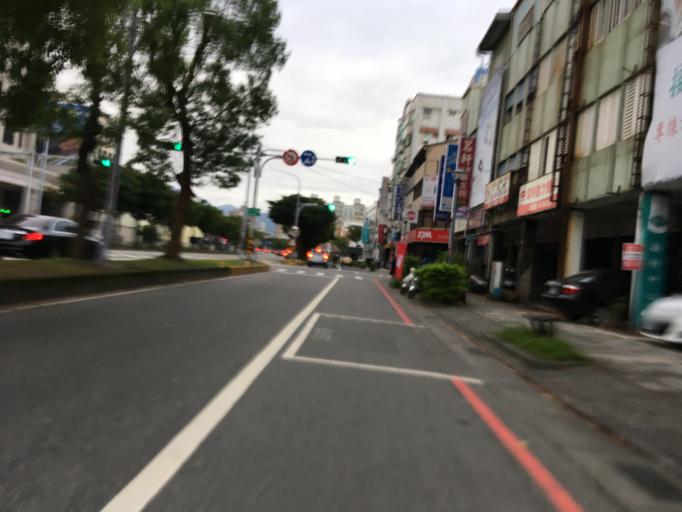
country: TW
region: Taiwan
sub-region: Yilan
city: Yilan
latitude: 24.6832
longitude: 121.7653
